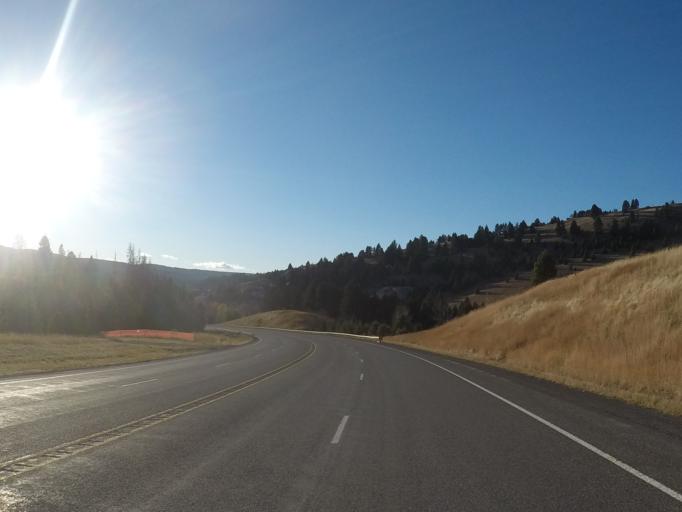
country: US
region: Montana
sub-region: Lewis and Clark County
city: Helena West Side
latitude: 46.5629
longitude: -112.3765
